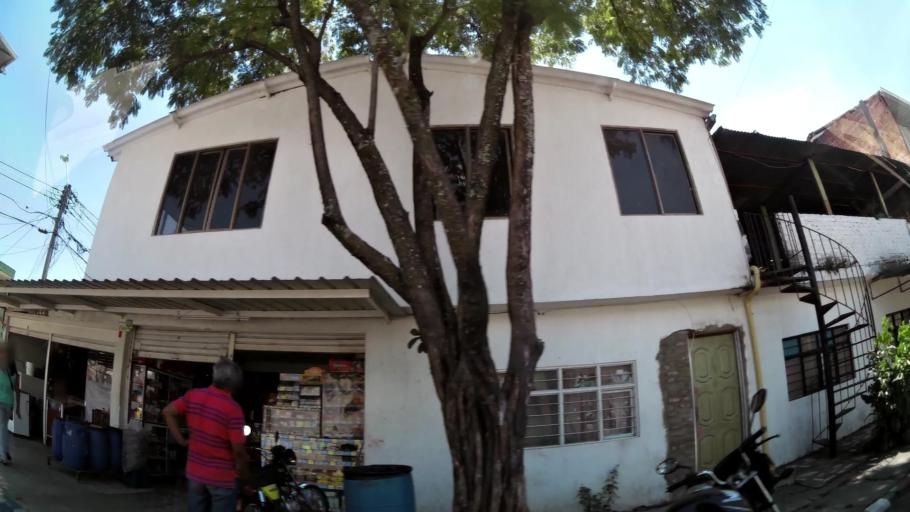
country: CO
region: Valle del Cauca
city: Cali
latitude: 3.4352
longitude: -76.5019
